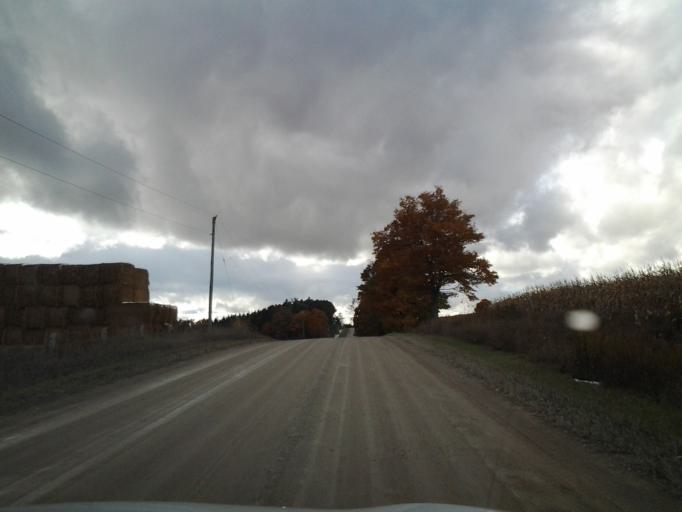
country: CA
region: Ontario
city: Shelburne
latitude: 44.0570
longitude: -80.1183
